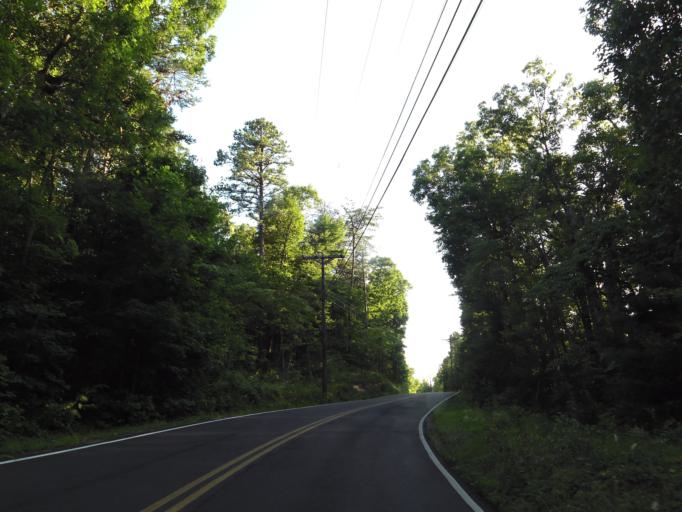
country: US
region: Tennessee
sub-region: Blount County
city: Maryville
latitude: 35.6395
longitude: -83.9227
